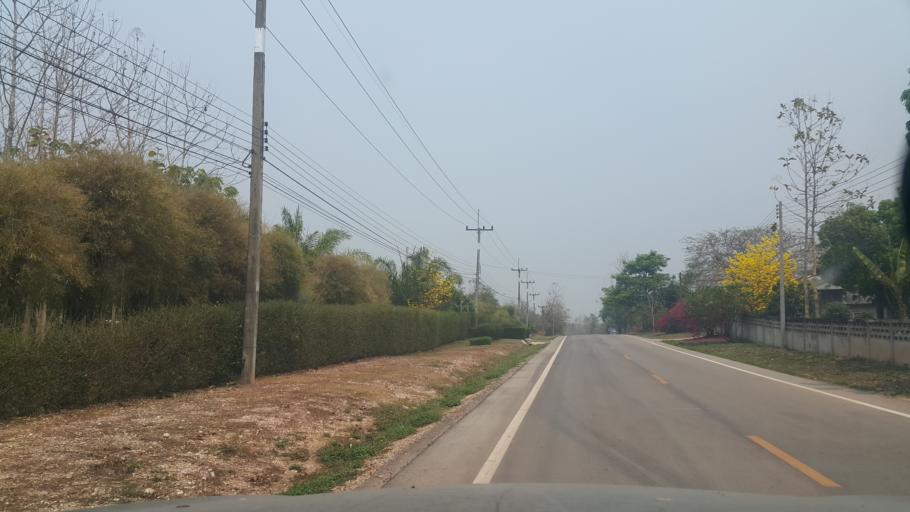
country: TH
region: Lampang
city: Hang Chat
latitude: 18.2320
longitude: 99.2310
